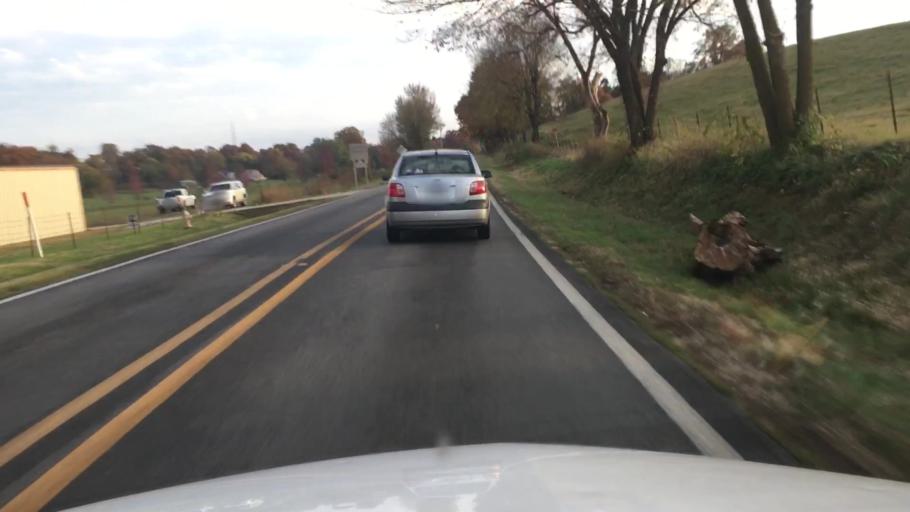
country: US
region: Arkansas
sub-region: Washington County
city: Elm Springs
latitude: 36.1999
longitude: -94.2313
